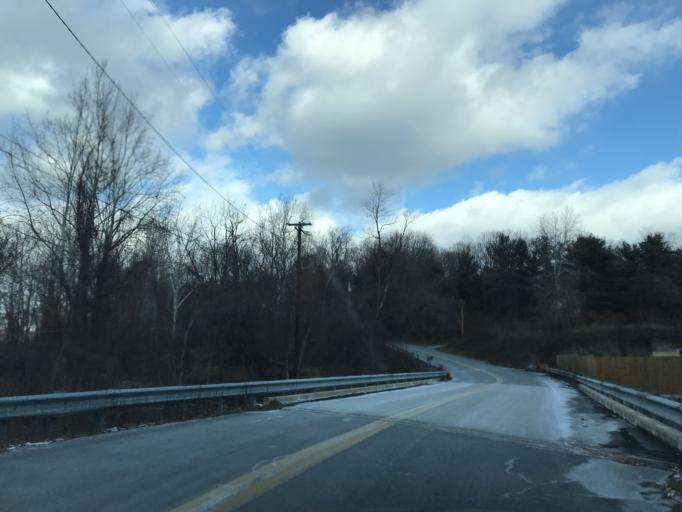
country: US
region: Maryland
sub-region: Baltimore County
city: Hunt Valley
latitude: 39.5542
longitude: -76.6653
